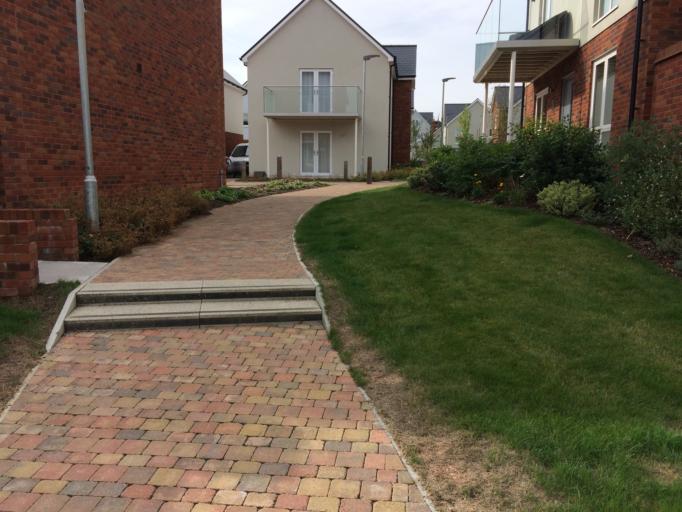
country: GB
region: England
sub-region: Kent
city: Pembury
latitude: 51.1528
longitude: 0.2939
